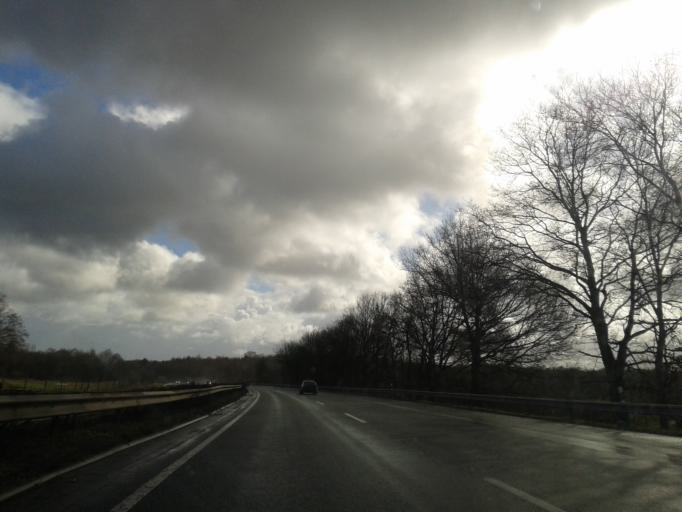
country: DE
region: Lower Saxony
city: Wiefelstede
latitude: 53.1648
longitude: 8.1250
